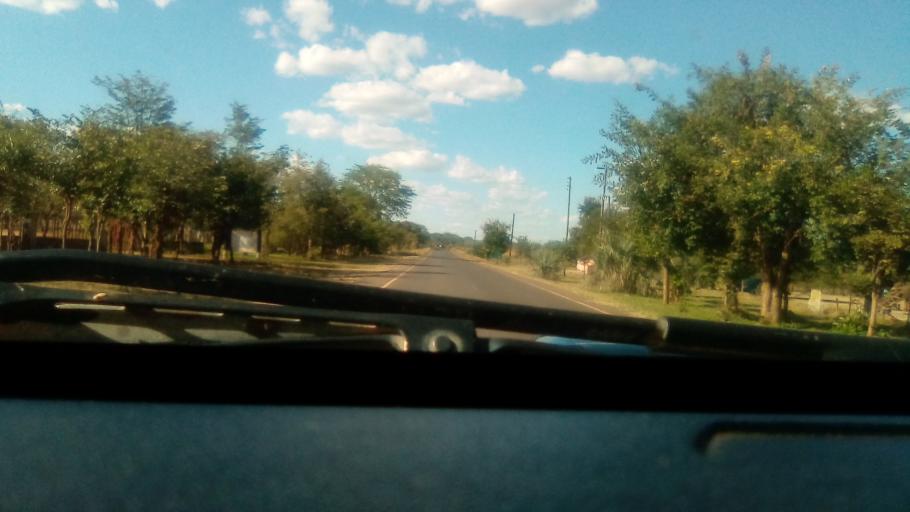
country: ZM
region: Southern
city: Livingstone
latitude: -17.8804
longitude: 25.8477
